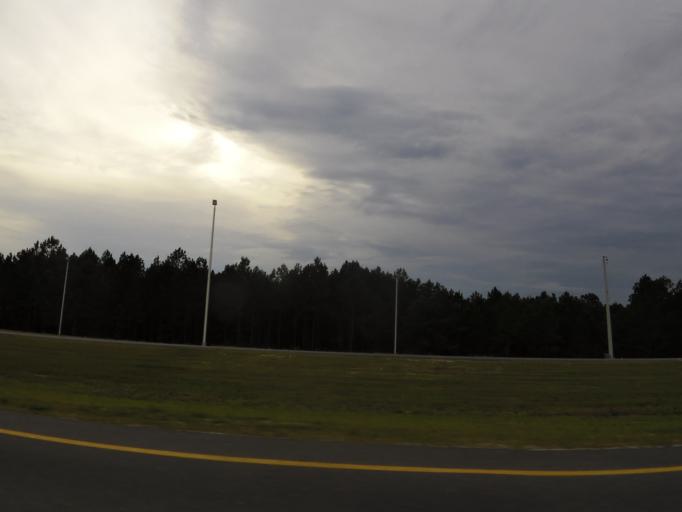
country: US
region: Florida
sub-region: Clay County
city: Lakeside
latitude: 30.1915
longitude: -81.8373
